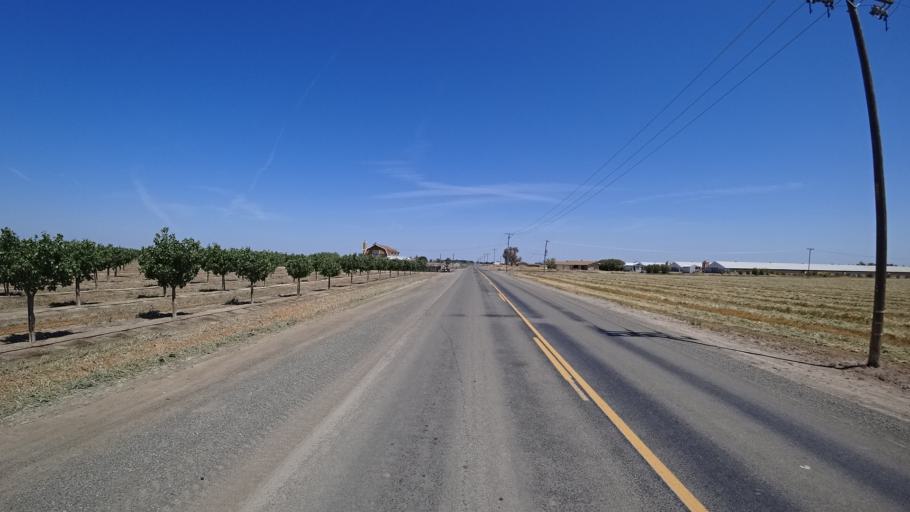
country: US
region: California
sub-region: Kings County
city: Stratford
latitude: 36.2321
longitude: -119.7984
